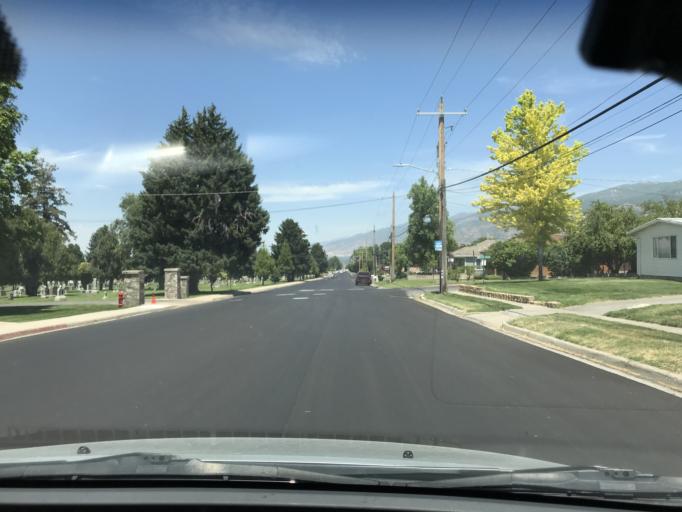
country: US
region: Utah
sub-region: Davis County
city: Woods Cross
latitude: 40.8659
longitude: -111.8857
